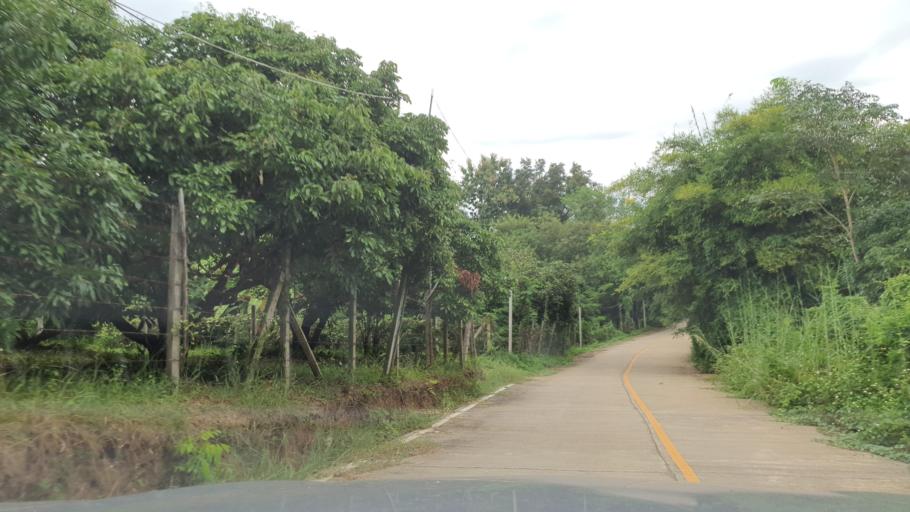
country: TH
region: Chiang Mai
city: San Sai
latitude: 18.9350
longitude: 98.9063
